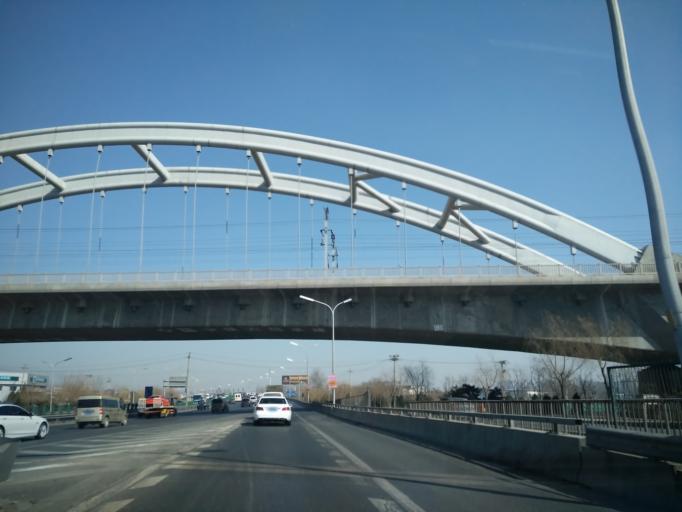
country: CN
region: Beijing
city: Jiugong
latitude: 39.8436
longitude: 116.4764
